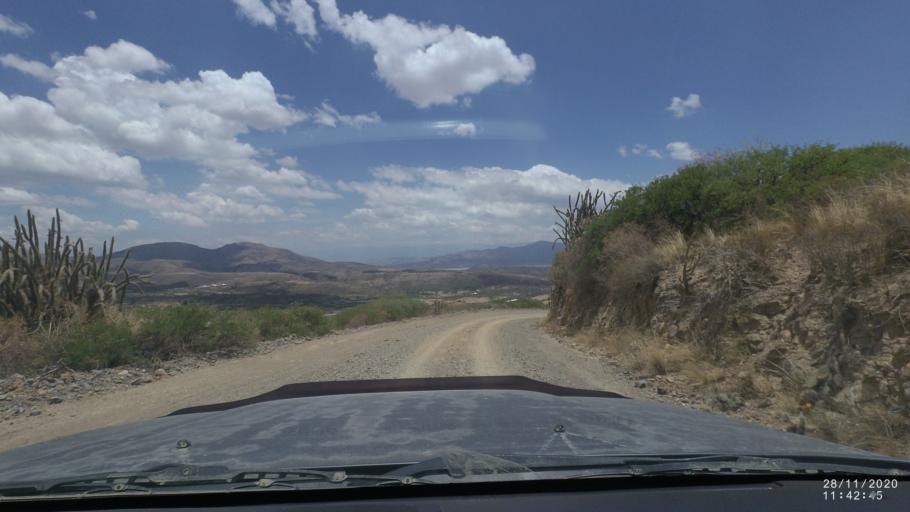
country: BO
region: Cochabamba
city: Tarata
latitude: -17.6627
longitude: -66.0466
